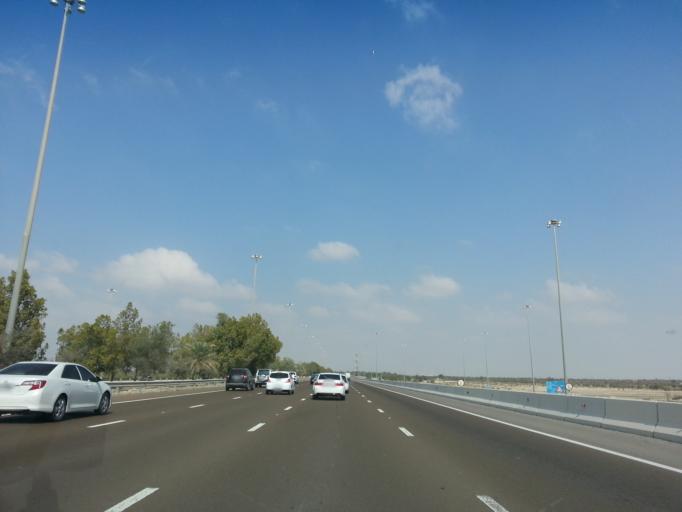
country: AE
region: Dubai
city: Dubai
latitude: 24.7266
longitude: 54.8141
